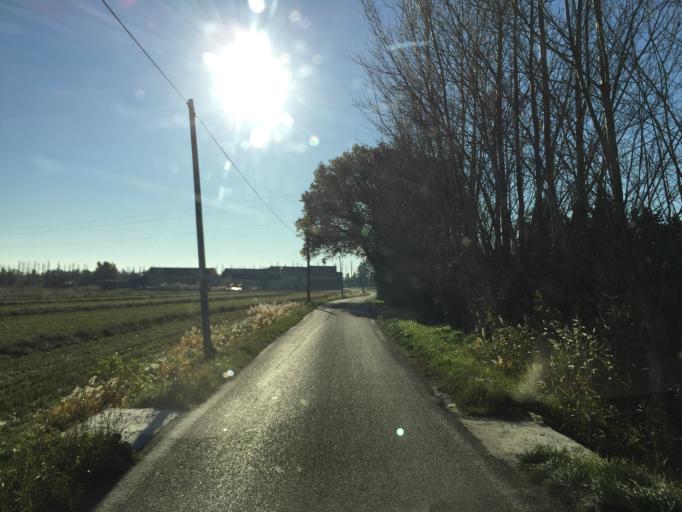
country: FR
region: Provence-Alpes-Cote d'Azur
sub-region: Departement du Vaucluse
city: Bedarrides
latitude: 44.0546
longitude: 4.9316
